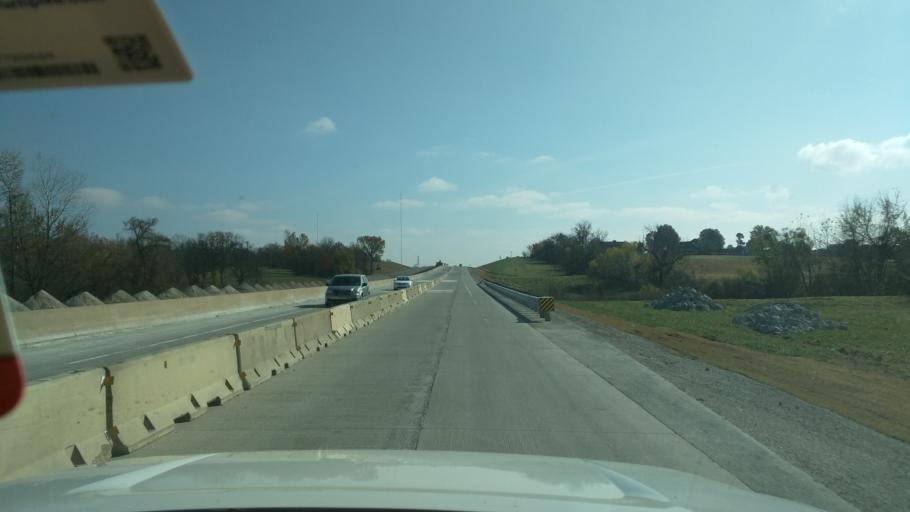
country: US
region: Oklahoma
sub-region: Tulsa County
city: Broken Arrow
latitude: 36.0398
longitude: -95.7225
